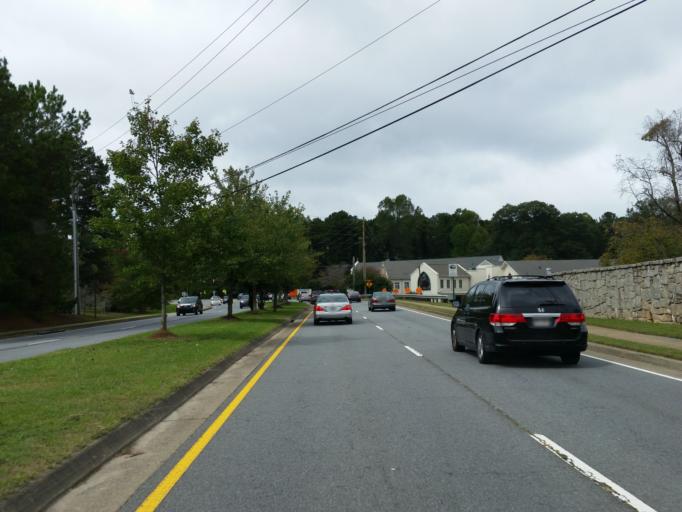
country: US
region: Georgia
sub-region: Fulton County
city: Roswell
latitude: 33.9913
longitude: -84.4281
